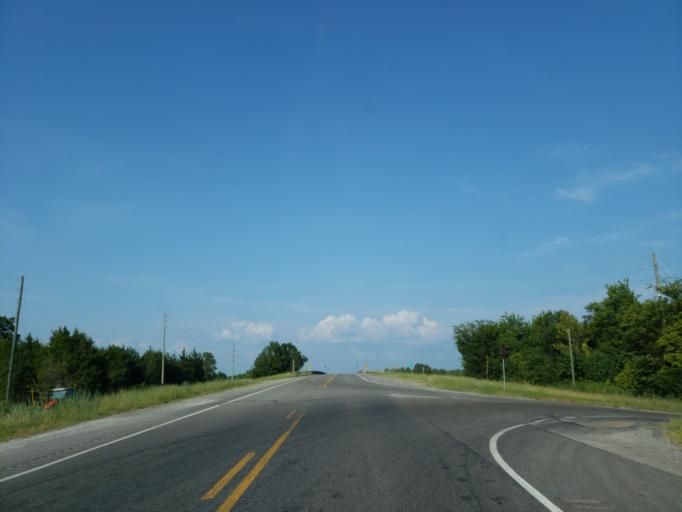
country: US
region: Alabama
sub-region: Sumter County
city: Livingston
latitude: 32.6934
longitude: -88.1166
